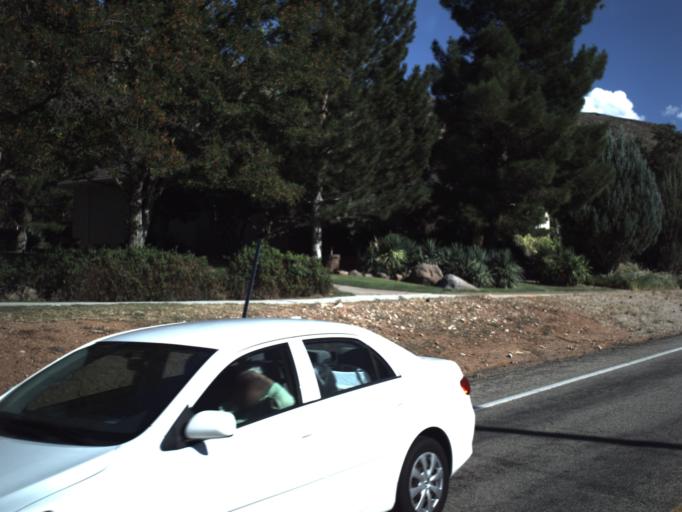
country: US
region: Utah
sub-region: Washington County
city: Toquerville
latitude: 37.2565
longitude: -113.2857
